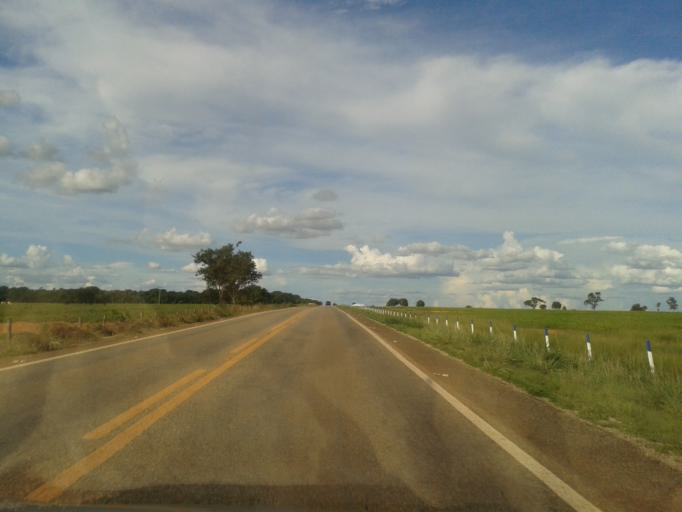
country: BR
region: Goias
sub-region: Mozarlandia
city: Mozarlandia
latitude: -14.3392
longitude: -50.4176
